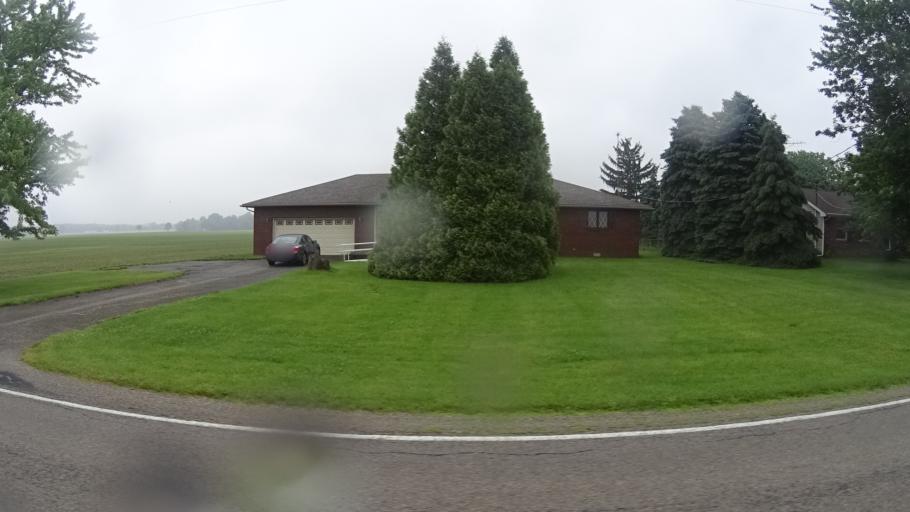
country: US
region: Ohio
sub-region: Huron County
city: Bellevue
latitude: 41.3627
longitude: -82.8446
